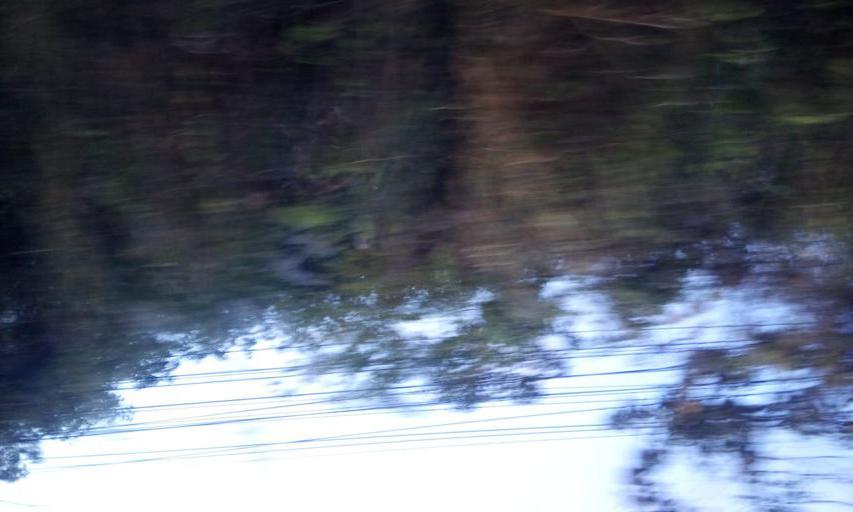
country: TH
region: Trat
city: Laem Ngop
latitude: 12.2611
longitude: 102.2919
